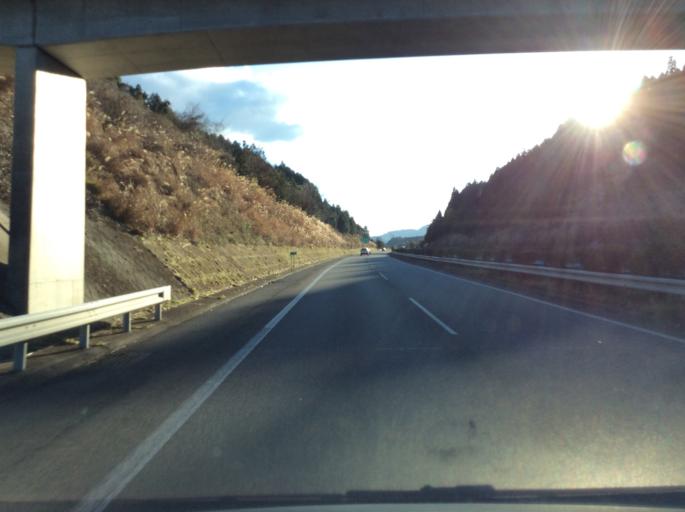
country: JP
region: Ibaraki
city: Kitaibaraki
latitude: 36.9141
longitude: 140.7573
